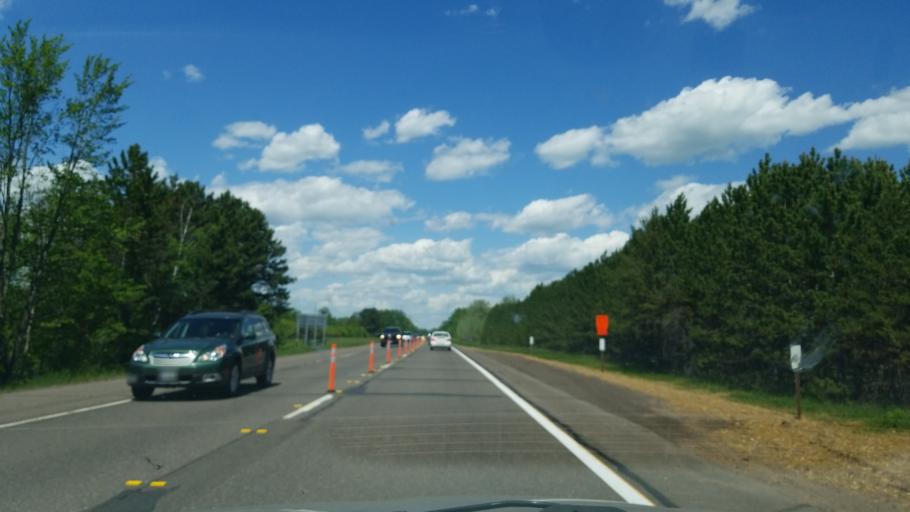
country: US
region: Minnesota
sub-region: Carlton County
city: Moose Lake
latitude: 46.3818
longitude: -92.7845
